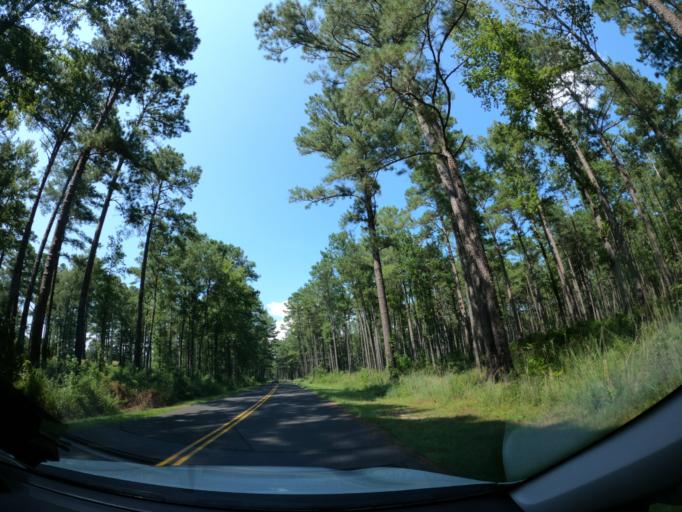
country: US
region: South Carolina
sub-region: Richland County
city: Gadsden
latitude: 33.8380
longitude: -80.8288
